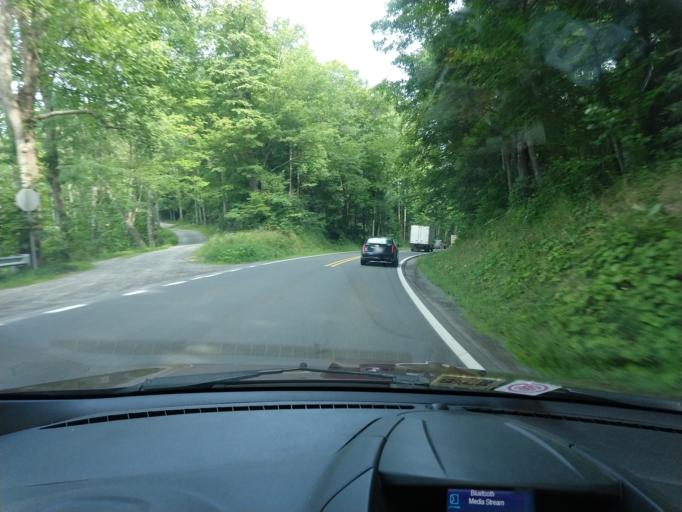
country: US
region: West Virginia
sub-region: Nicholas County
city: Craigsville
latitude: 38.2554
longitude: -80.7268
